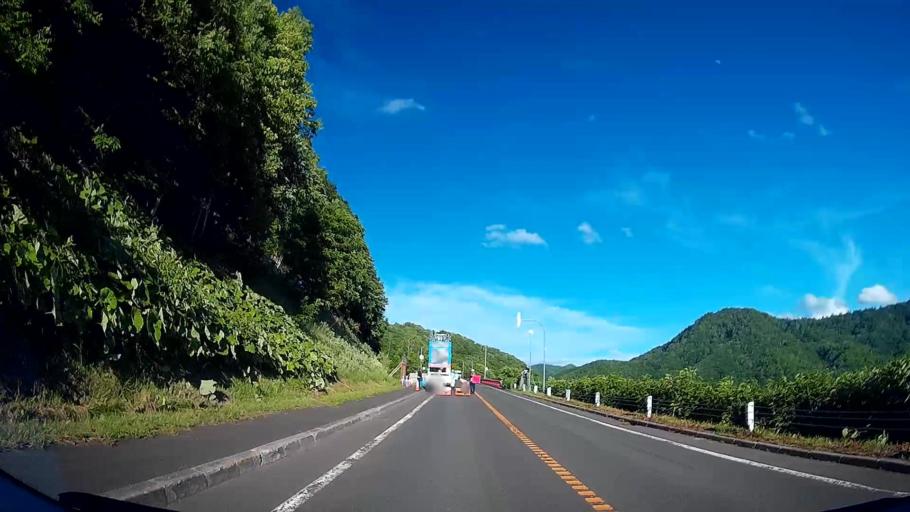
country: JP
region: Hokkaido
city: Sapporo
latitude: 42.9776
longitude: 141.1410
